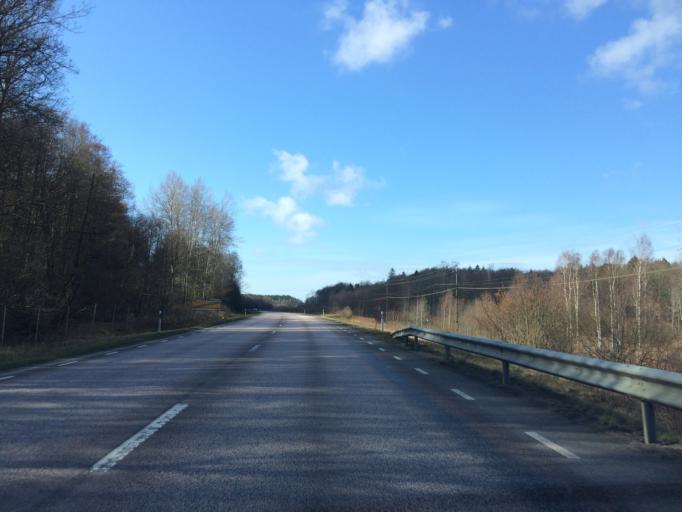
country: SE
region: Halland
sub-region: Laholms Kommun
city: Knared
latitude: 56.5172
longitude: 13.3032
